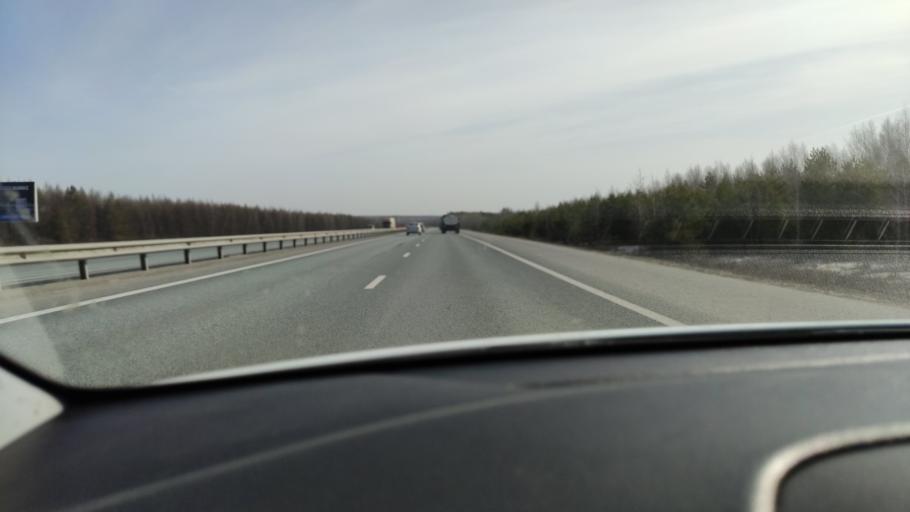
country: RU
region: Tatarstan
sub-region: Gorod Kazan'
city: Kazan
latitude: 55.9124
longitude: 49.0944
